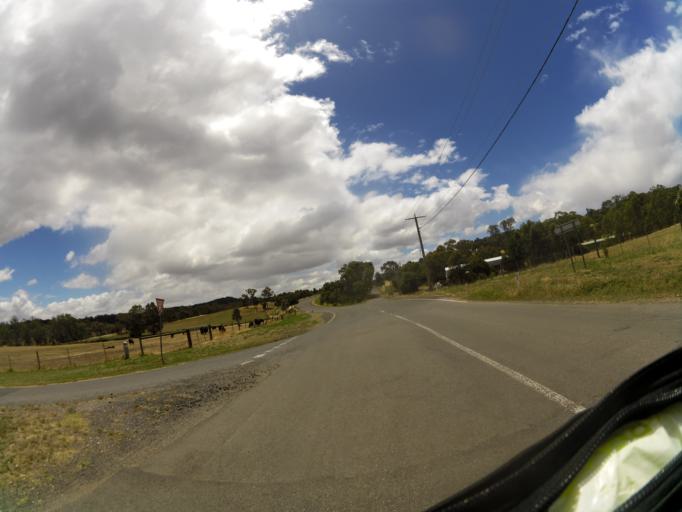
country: AU
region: Victoria
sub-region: Mount Alexander
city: Castlemaine
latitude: -37.0130
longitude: 144.2511
